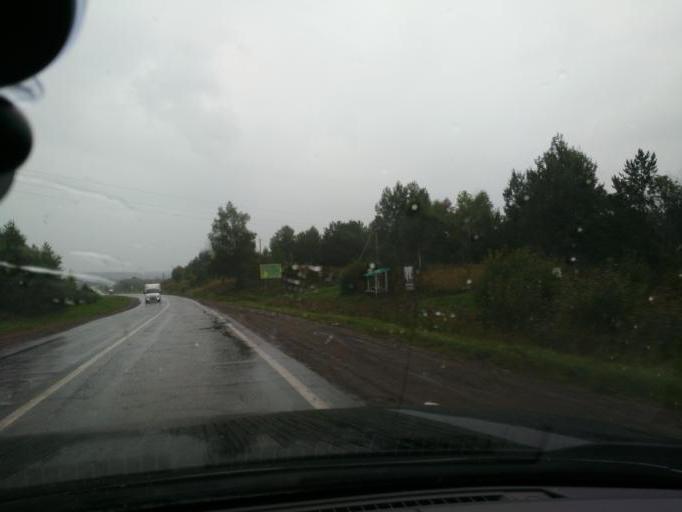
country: RU
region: Perm
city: Barda
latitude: 56.9444
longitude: 55.6306
